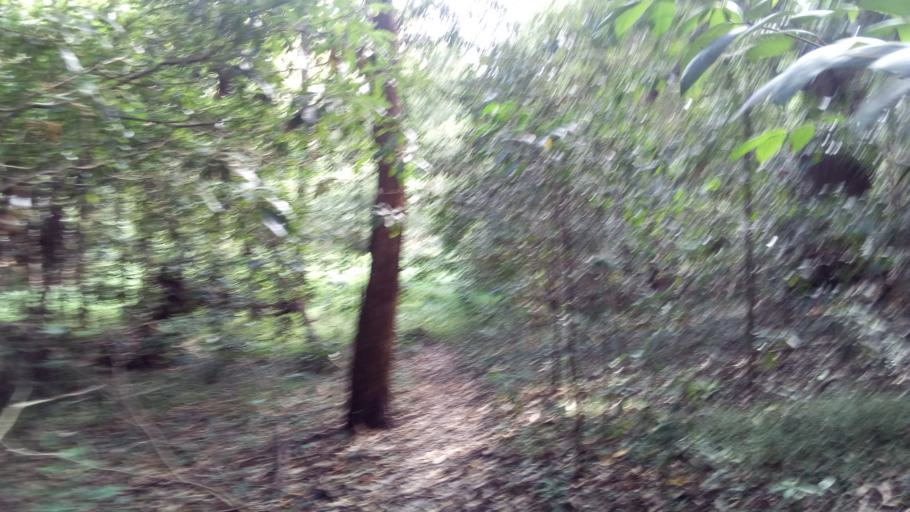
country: AU
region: New South Wales
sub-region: Wollongong
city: Mangerton
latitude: -34.4330
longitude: 150.8755
